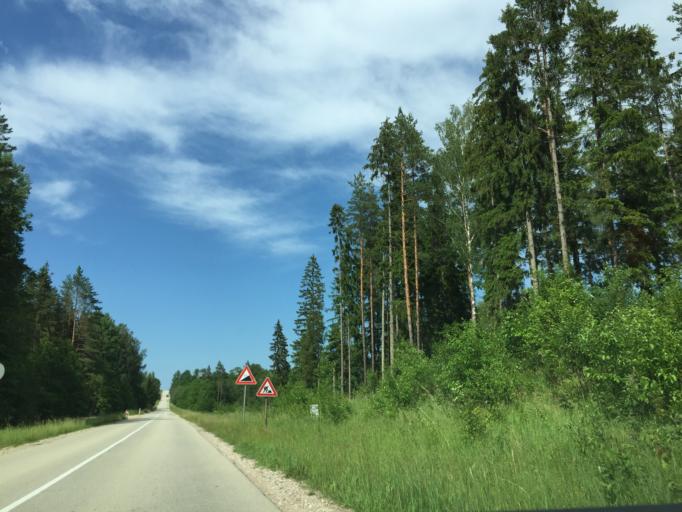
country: LV
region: Tukuma Rajons
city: Tukums
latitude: 57.0243
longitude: 23.2498
